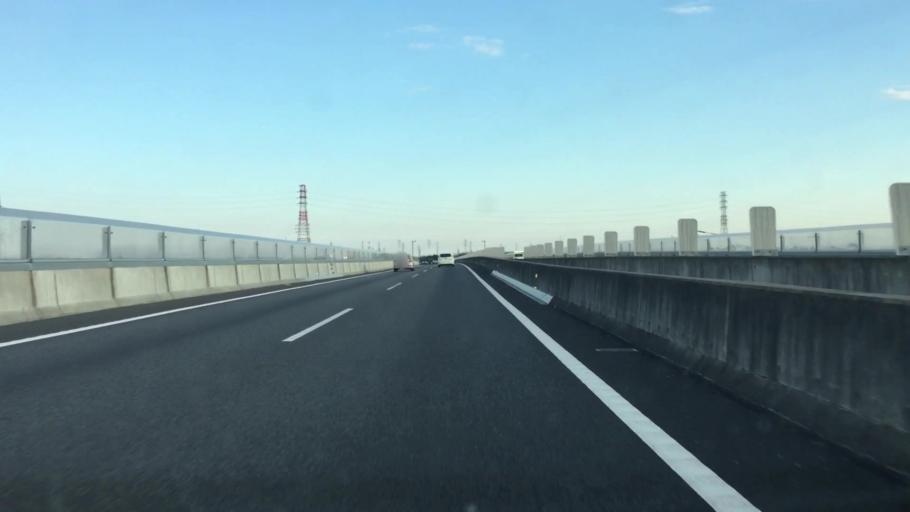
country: JP
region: Gunma
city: Isesaki
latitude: 36.3466
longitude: 139.2473
